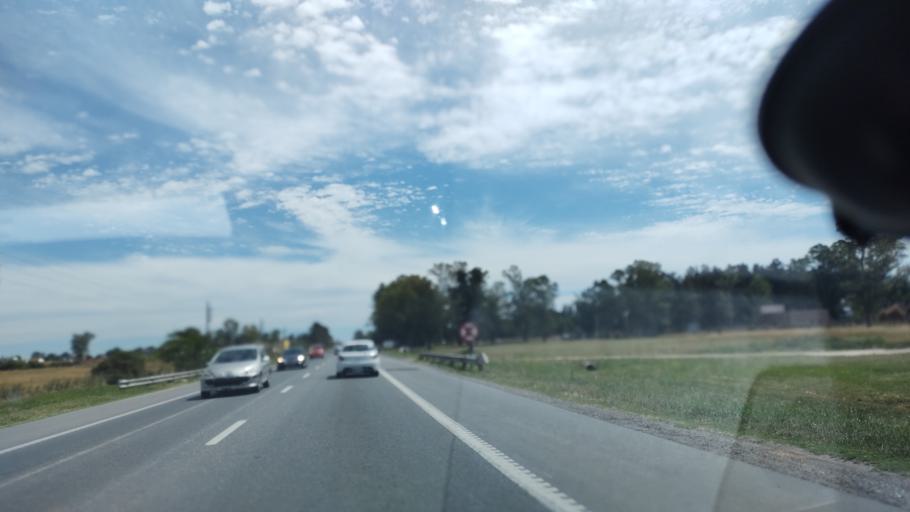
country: AR
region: Buenos Aires
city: Canuelas
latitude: -35.0331
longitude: -58.7529
